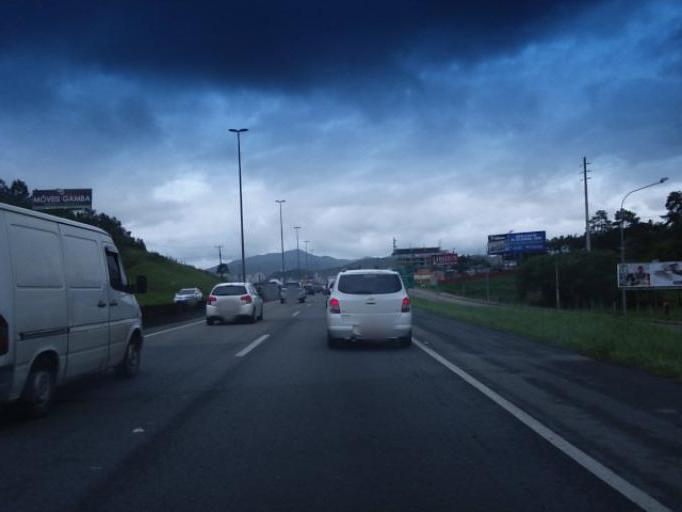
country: BR
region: Santa Catarina
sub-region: Balneario Camboriu
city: Balneario Camboriu
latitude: -26.9894
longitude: -48.6640
